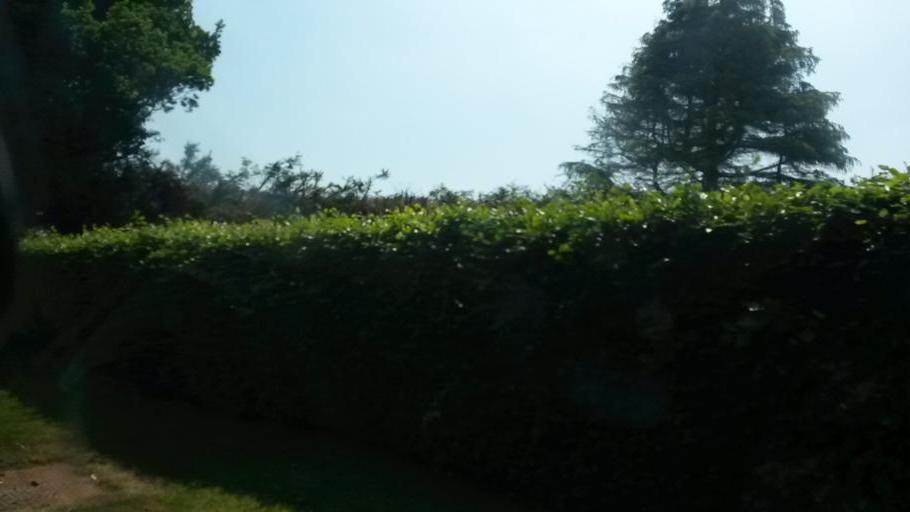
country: IE
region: Leinster
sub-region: An Mhi
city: Slane
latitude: 53.7170
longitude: -6.5344
